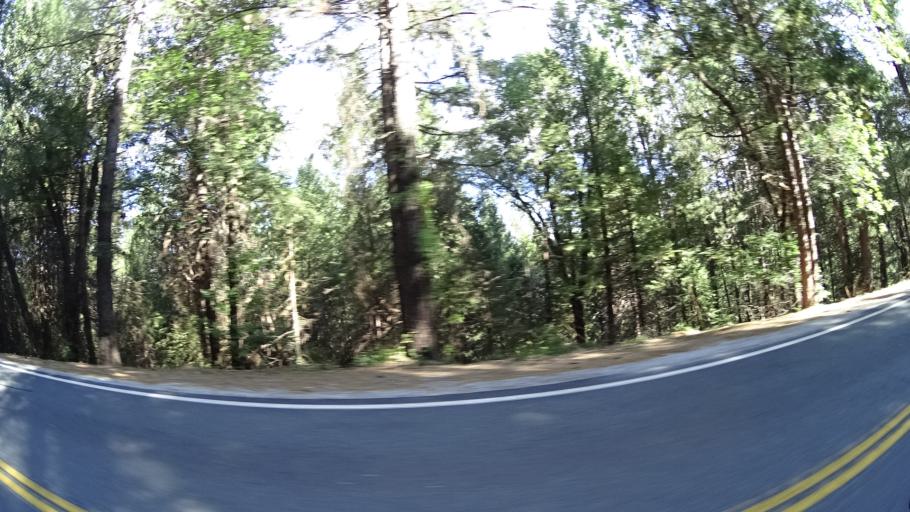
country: US
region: California
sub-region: Amador County
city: Pioneer
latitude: 38.3890
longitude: -120.5318
